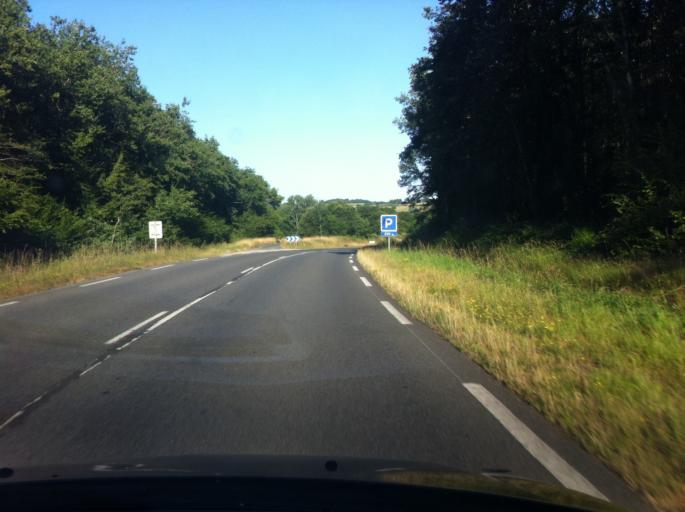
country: FR
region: Auvergne
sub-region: Departement de l'Allier
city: Chantelle
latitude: 46.3215
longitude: 3.0972
